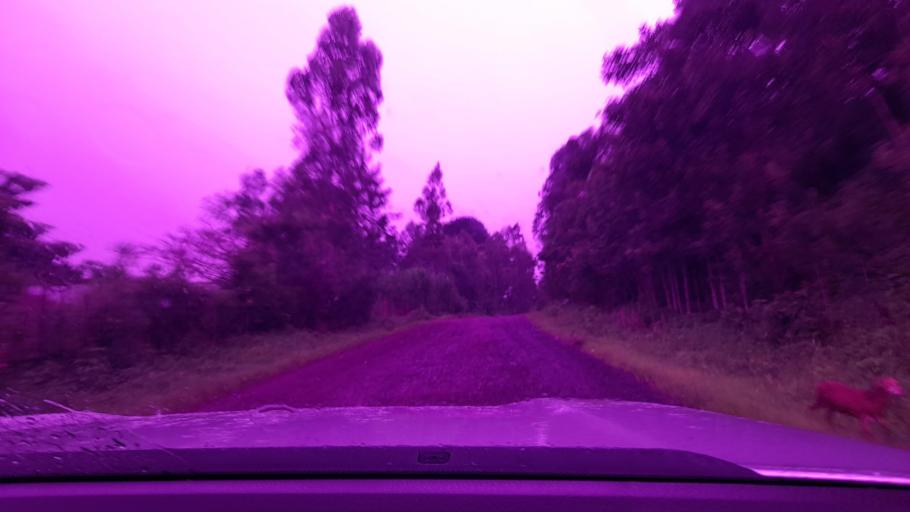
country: ET
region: Oromiya
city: Metu
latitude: 8.4552
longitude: 35.6372
